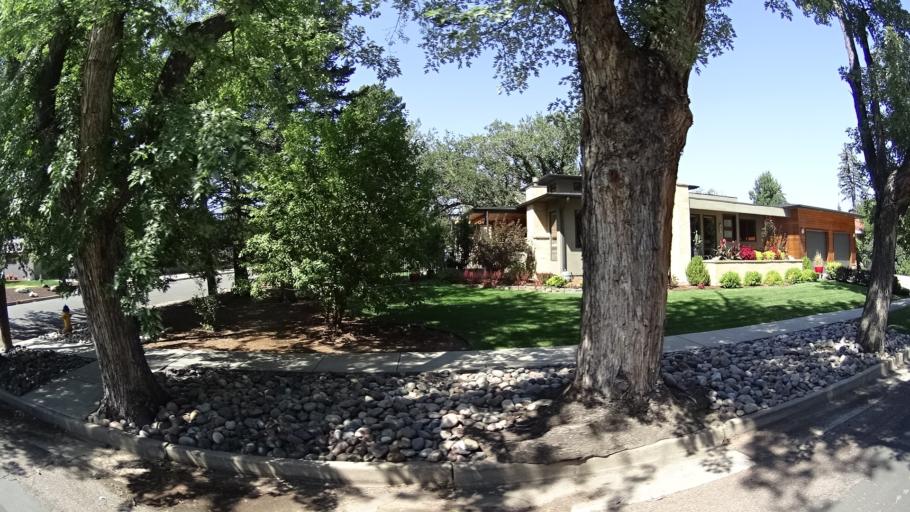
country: US
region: Colorado
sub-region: El Paso County
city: Colorado Springs
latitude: 38.8581
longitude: -104.8291
